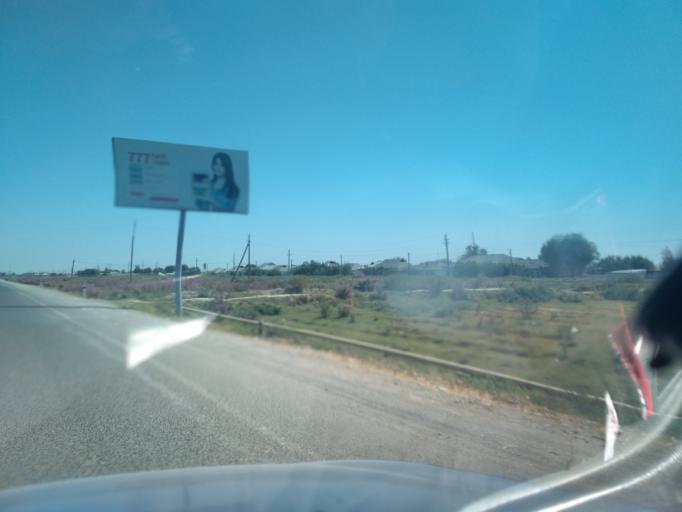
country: UZ
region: Sirdaryo
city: Guliston
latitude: 40.4916
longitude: 68.6978
